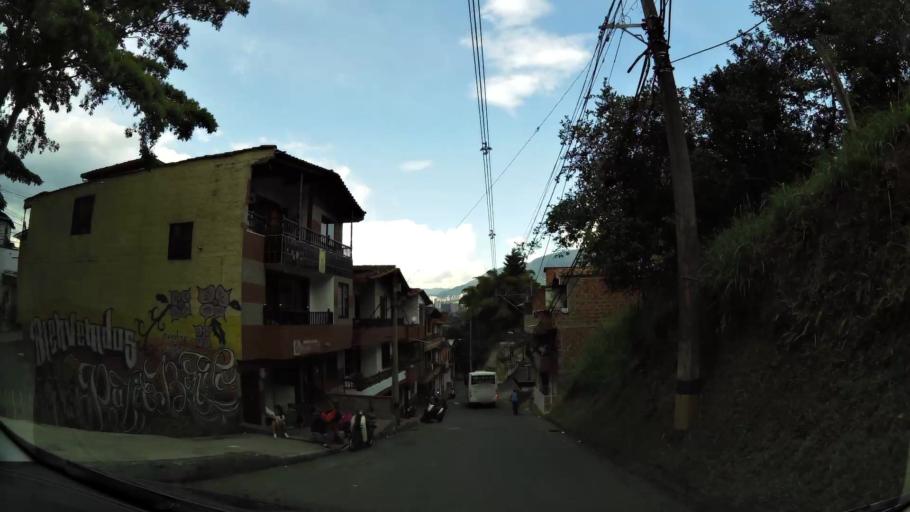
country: CO
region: Antioquia
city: Envigado
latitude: 6.1557
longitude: -75.5834
